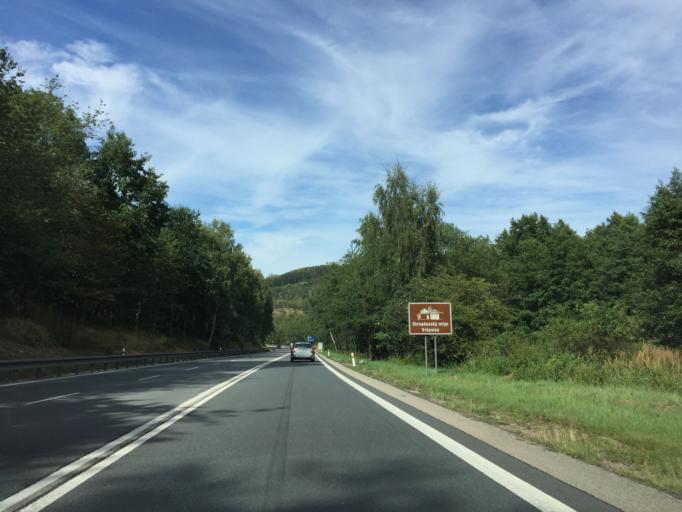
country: CZ
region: Central Bohemia
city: Votice
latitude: 49.6325
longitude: 14.6511
